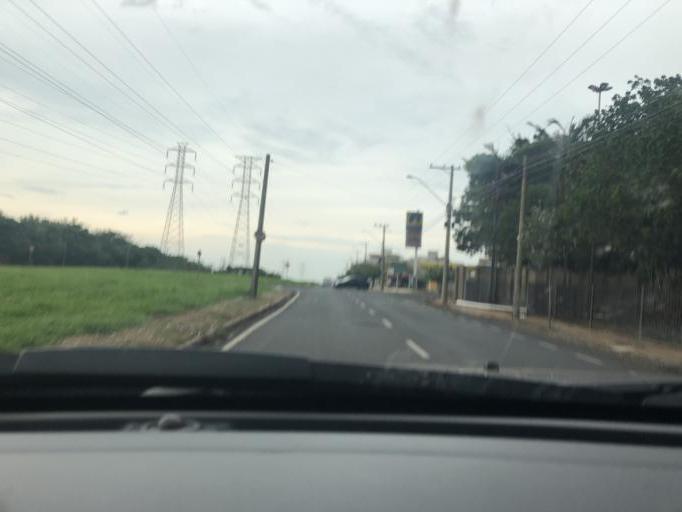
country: BR
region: Sao Paulo
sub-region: Sao Jose Do Rio Preto
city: Sao Jose do Rio Preto
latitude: -20.8445
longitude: -49.3901
